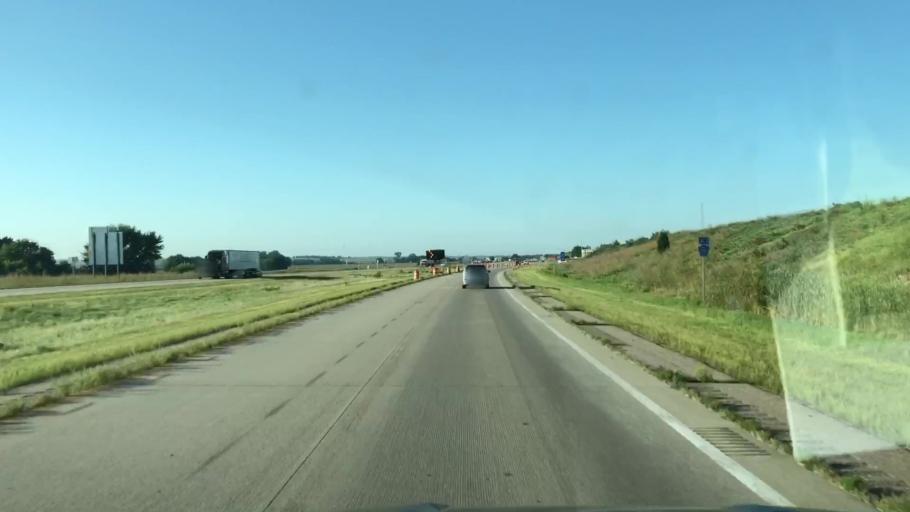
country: US
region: Iowa
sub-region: Plymouth County
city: Le Mars
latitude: 42.7534
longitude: -96.2101
